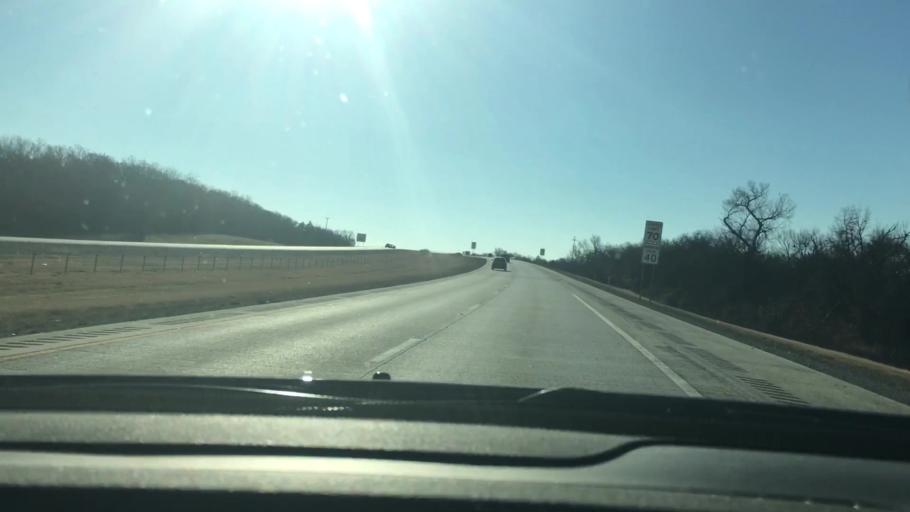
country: US
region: Oklahoma
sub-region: Carter County
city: Ardmore
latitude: 34.1622
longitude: -97.1659
